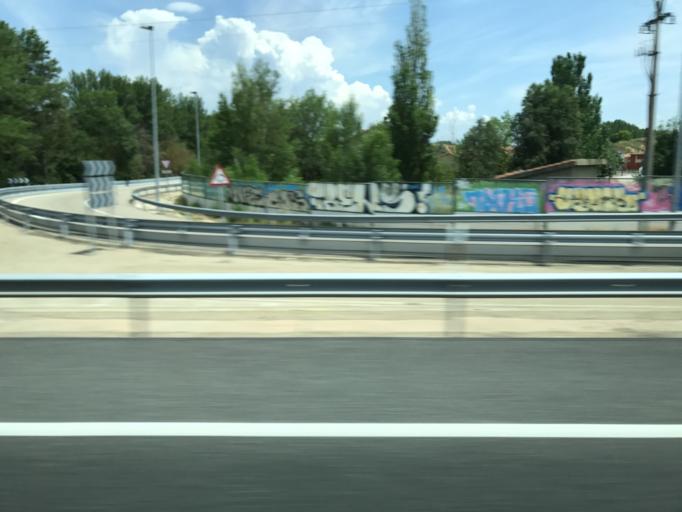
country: ES
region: Castille and Leon
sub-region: Provincia de Burgos
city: Saldana de Burgos
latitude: 42.2610
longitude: -3.6991
